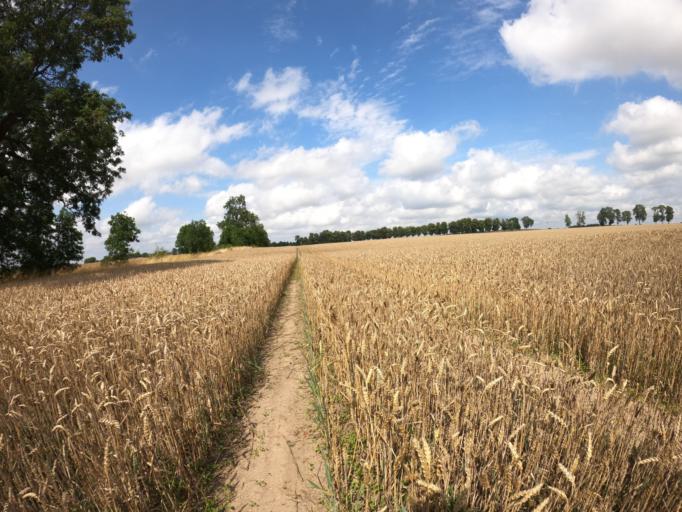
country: PL
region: West Pomeranian Voivodeship
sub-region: Powiat szczecinecki
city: Grzmiaca
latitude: 53.8099
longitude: 16.4708
